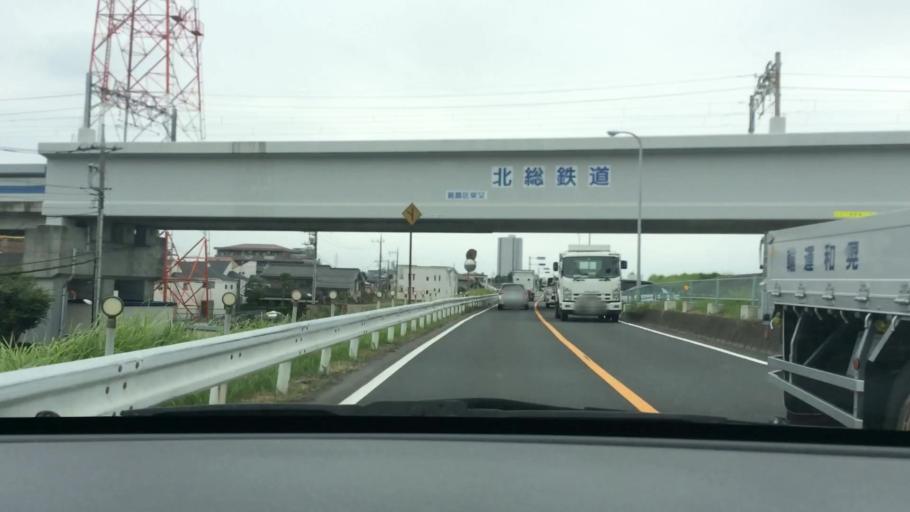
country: JP
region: Chiba
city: Matsudo
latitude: 35.7527
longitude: 139.8842
